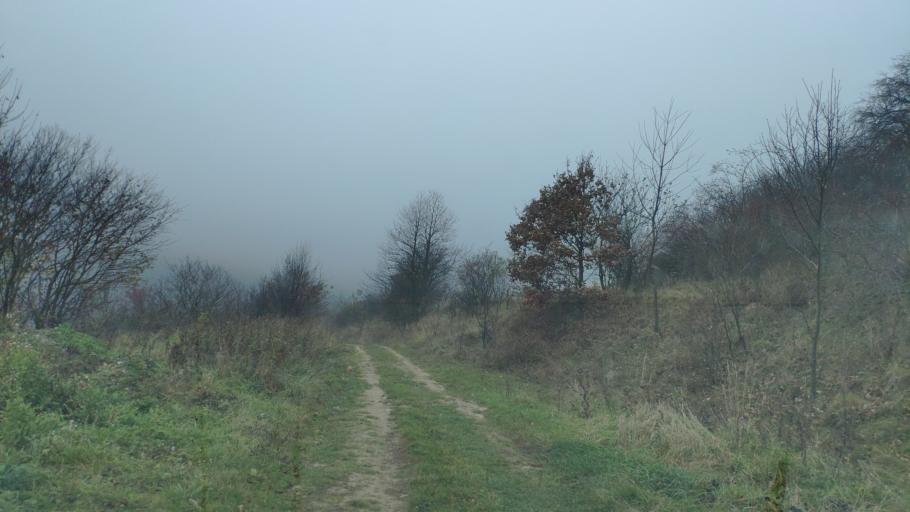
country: SK
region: Presovsky
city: Sabinov
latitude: 49.1404
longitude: 21.2215
